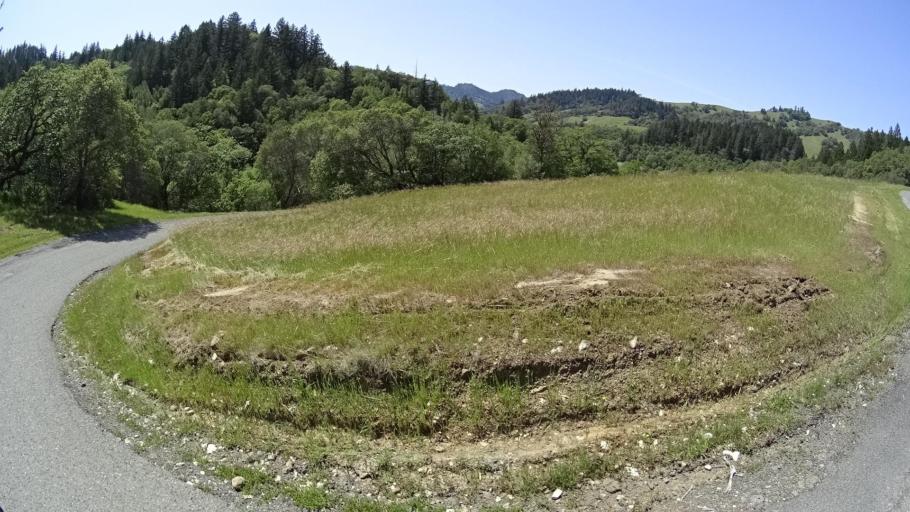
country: US
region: California
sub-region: Humboldt County
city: Redway
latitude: 40.2365
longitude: -123.6327
